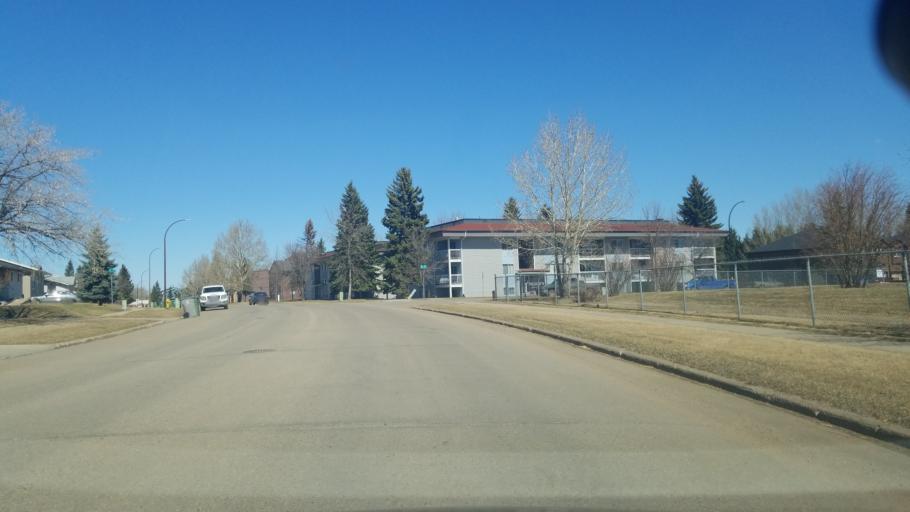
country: CA
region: Saskatchewan
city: Lloydminster
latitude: 53.2651
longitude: -110.0127
